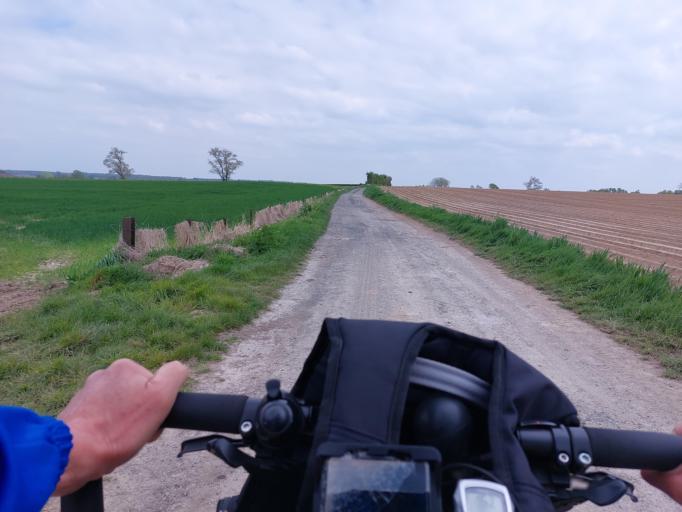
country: FR
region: Nord-Pas-de-Calais
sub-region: Departement du Nord
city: La Longueville
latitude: 50.2924
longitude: 3.8256
